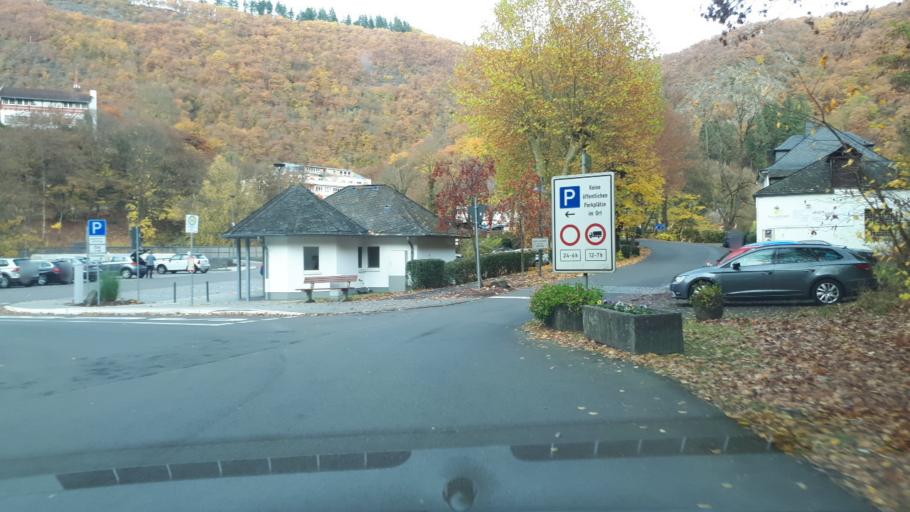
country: DE
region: Rheinland-Pfalz
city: Bad Bertrich
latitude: 50.0692
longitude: 7.0389
